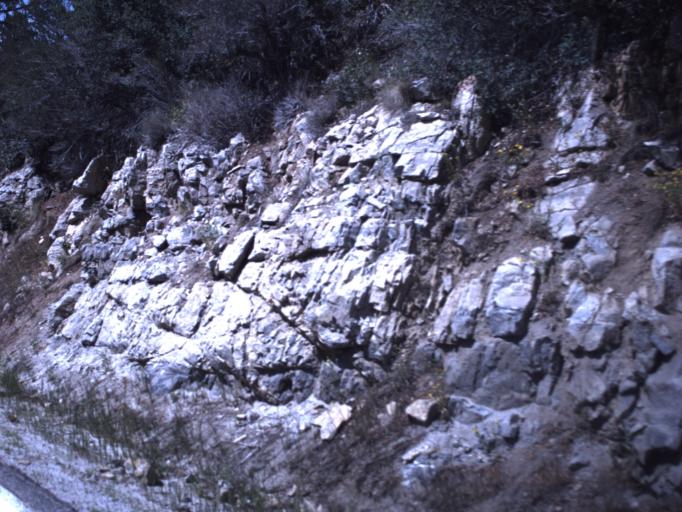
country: US
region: Idaho
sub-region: Bear Lake County
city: Paris
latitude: 41.9591
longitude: -111.5145
